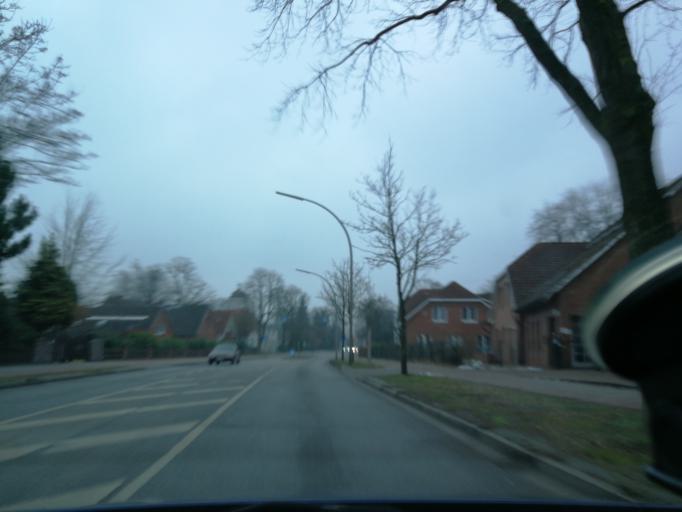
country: DE
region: Lower Saxony
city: Neu Wulmstorf
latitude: 53.4767
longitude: 9.8584
